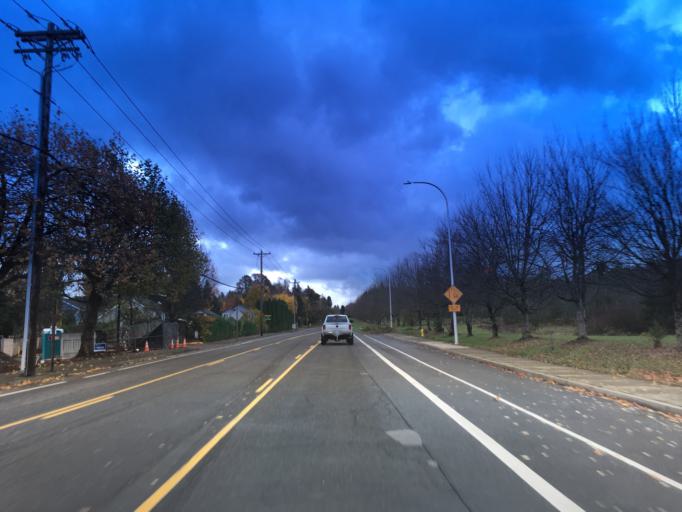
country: US
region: Oregon
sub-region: Multnomah County
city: Troutdale
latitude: 45.5182
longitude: -122.3870
